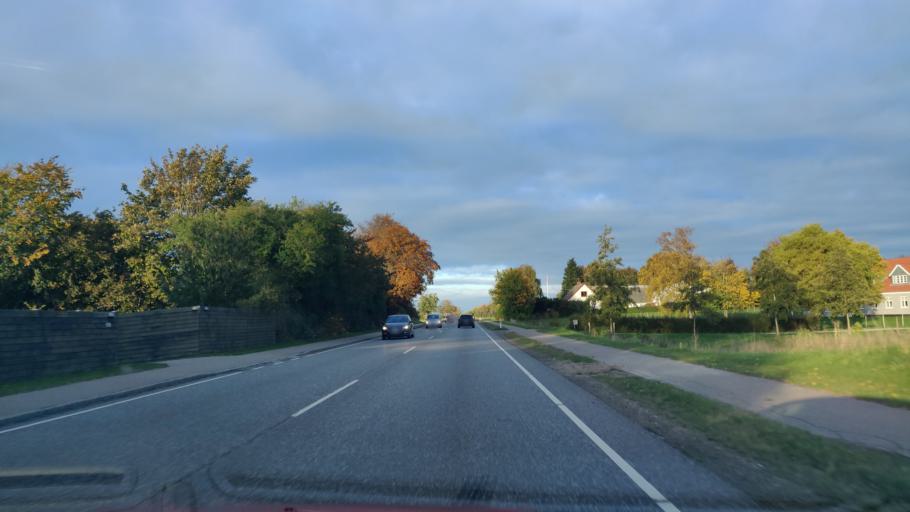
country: DK
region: Zealand
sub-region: Holbaek Kommune
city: Vipperod
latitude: 55.6616
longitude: 11.6810
